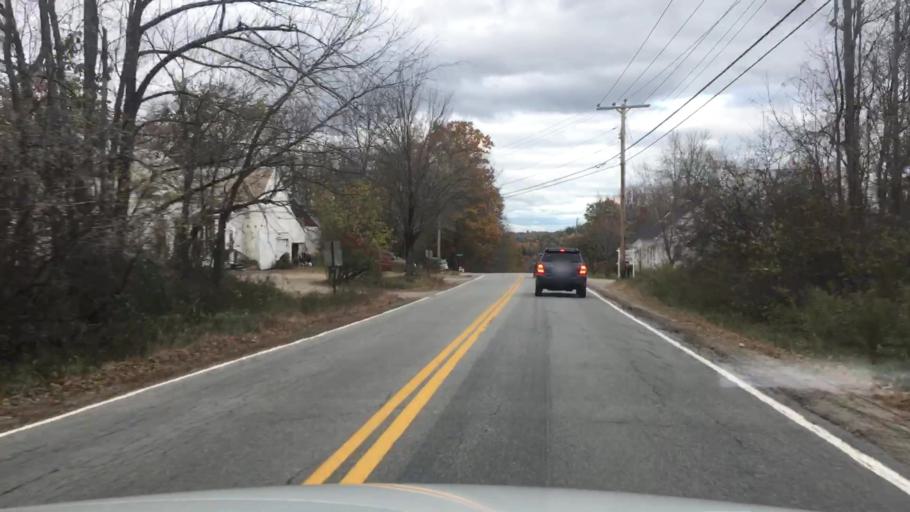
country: US
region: Maine
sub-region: Kennebec County
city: Monmouth
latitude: 44.1829
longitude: -70.0658
